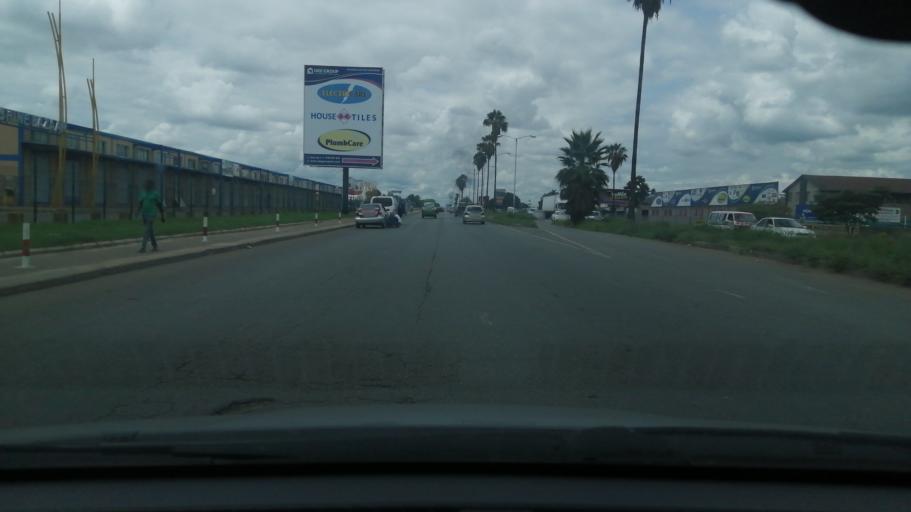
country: ZW
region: Harare
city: Harare
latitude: -17.8632
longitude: 31.0262
